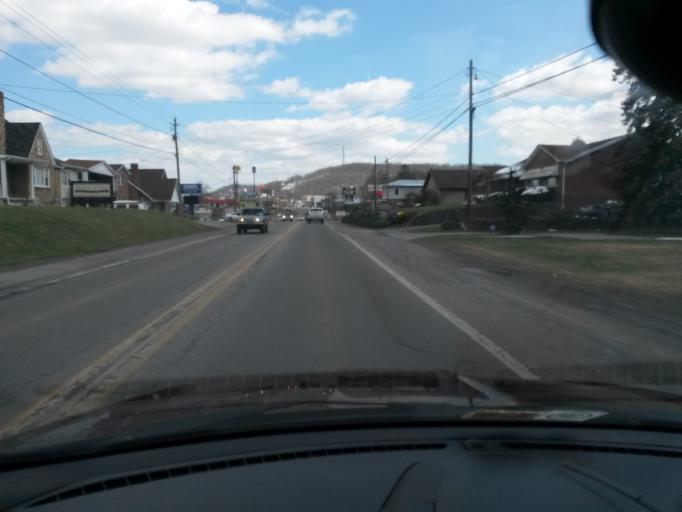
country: US
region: West Virginia
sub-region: Mercer County
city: Princeton
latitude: 37.3639
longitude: -81.0643
